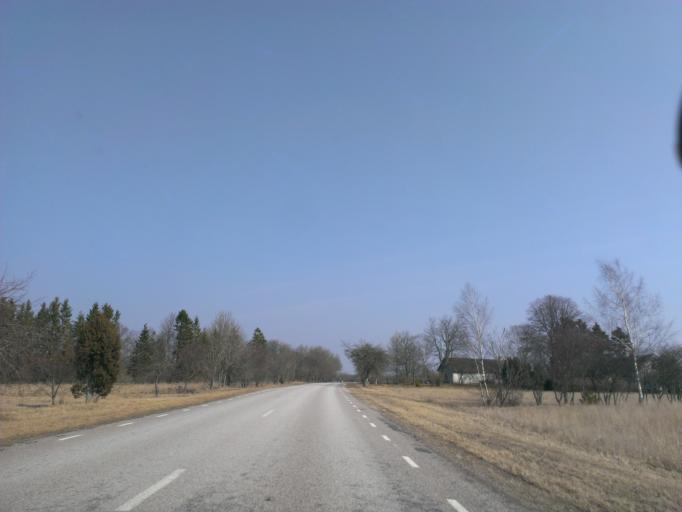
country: EE
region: Saare
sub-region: Kuressaare linn
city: Kuressaare
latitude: 58.2839
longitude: 22.6500
